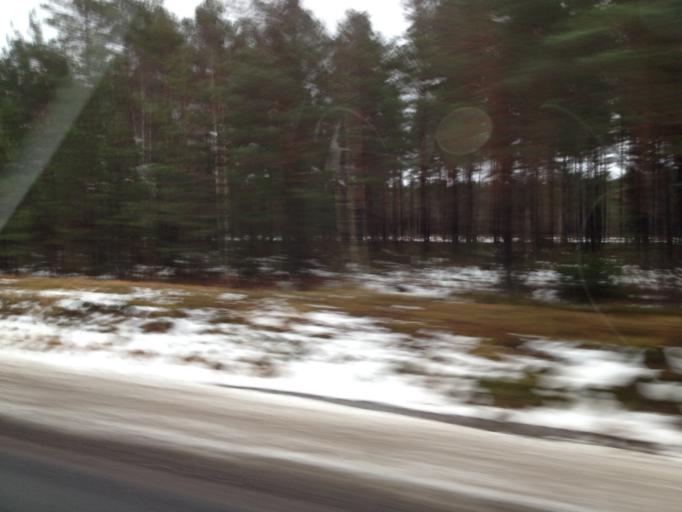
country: FI
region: Uusimaa
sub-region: Raaseporin
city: Ekenaes
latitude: 59.9238
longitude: 23.3014
